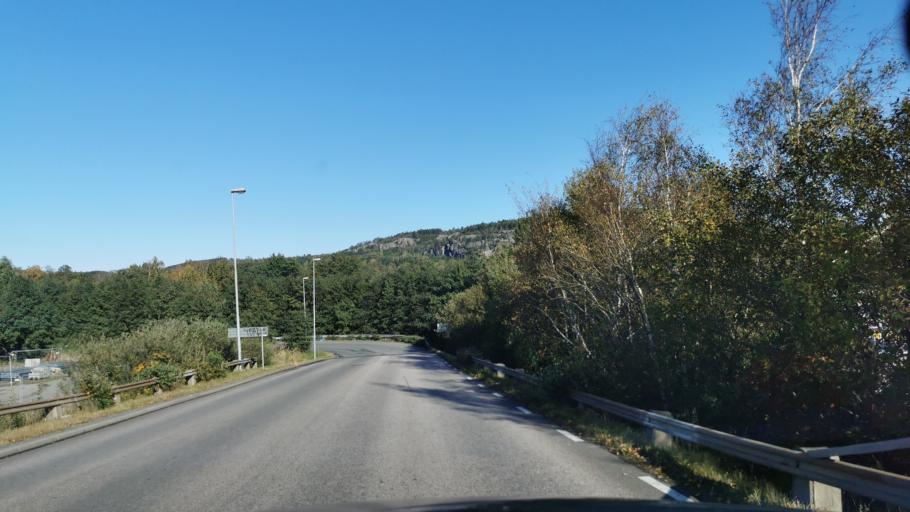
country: SE
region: Vaestra Goetaland
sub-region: Partille Kommun
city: Partille
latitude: 57.7335
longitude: 12.0665
